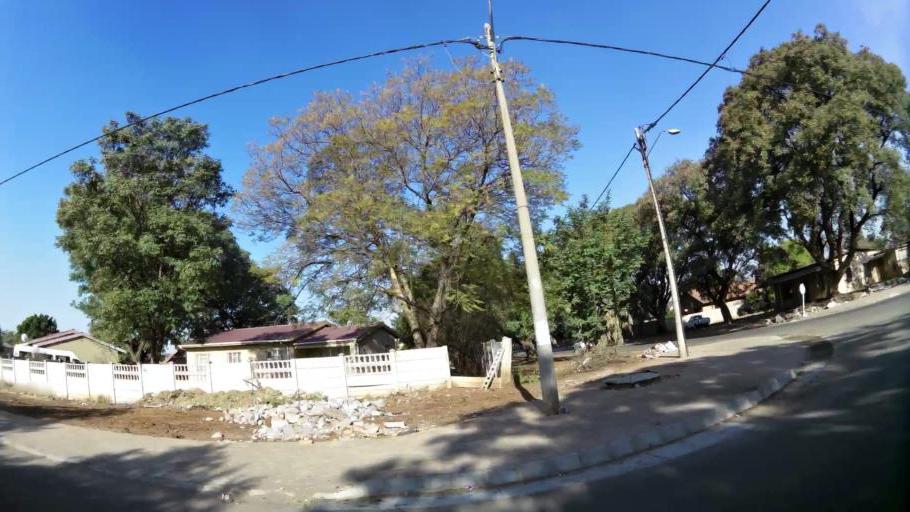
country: ZA
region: North-West
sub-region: Bojanala Platinum District Municipality
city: Rustenburg
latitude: -25.6556
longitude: 27.2294
